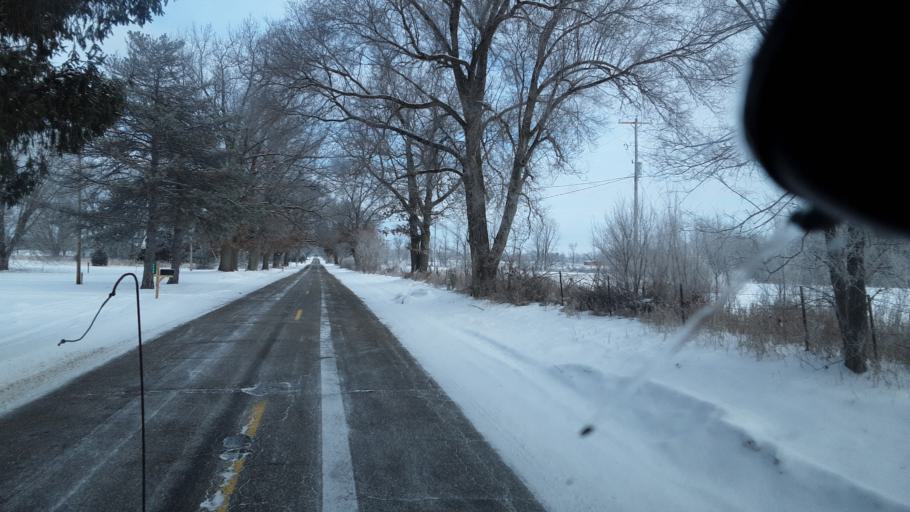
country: US
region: Michigan
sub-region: Ingham County
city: Leslie
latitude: 42.3789
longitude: -84.4924
